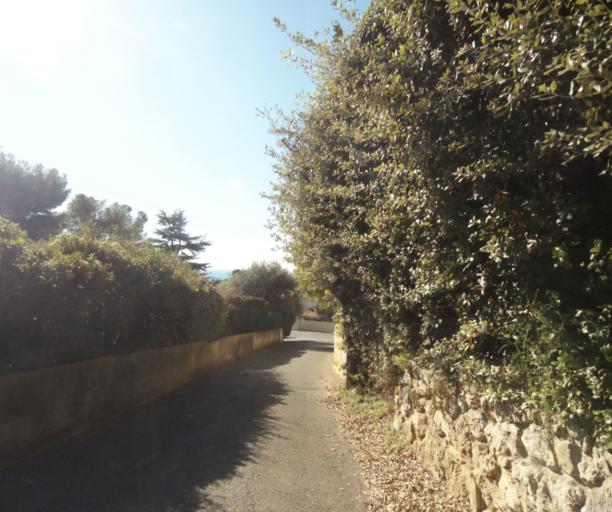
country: FR
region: Provence-Alpes-Cote d'Azur
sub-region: Departement des Alpes-Maritimes
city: Antibes
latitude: 43.5622
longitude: 7.1227
